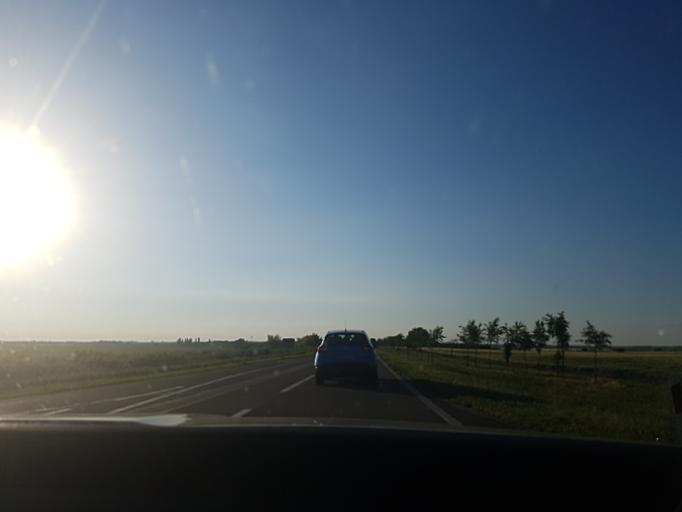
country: RO
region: Timis
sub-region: Comuna Moravita
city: Moravita
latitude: 45.2189
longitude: 21.2981
